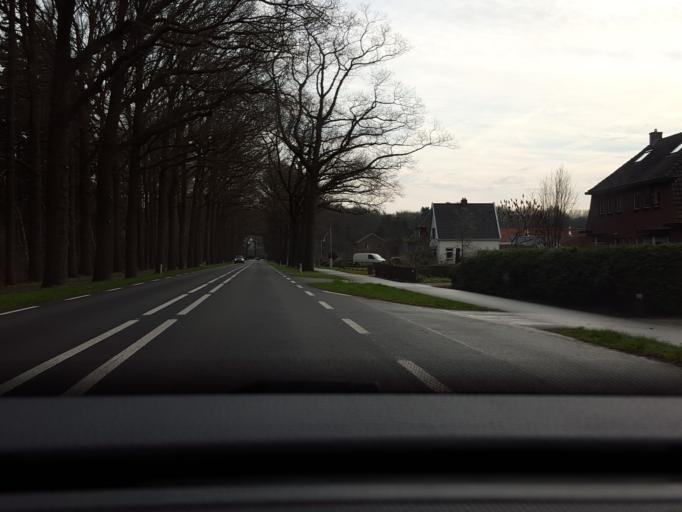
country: NL
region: Gelderland
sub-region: Gemeente Lochem
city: Almen
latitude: 52.1188
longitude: 6.2928
